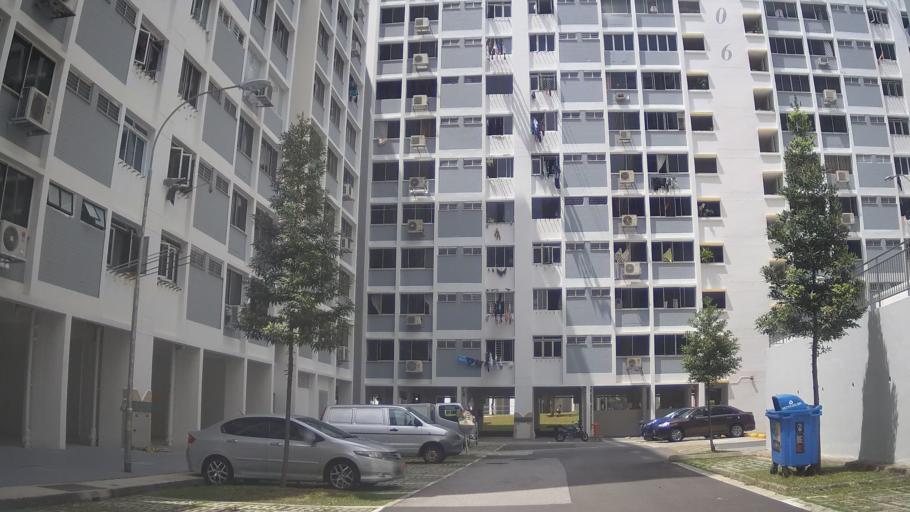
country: MY
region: Johor
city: Johor Bahru
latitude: 1.3815
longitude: 103.7676
